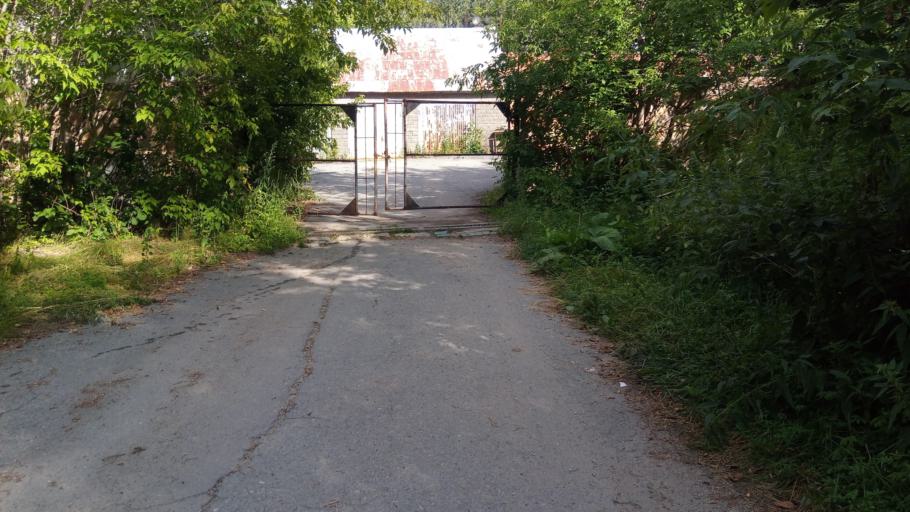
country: RU
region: Chelyabinsk
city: Chebarkul'
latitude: 55.0205
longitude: 60.3097
